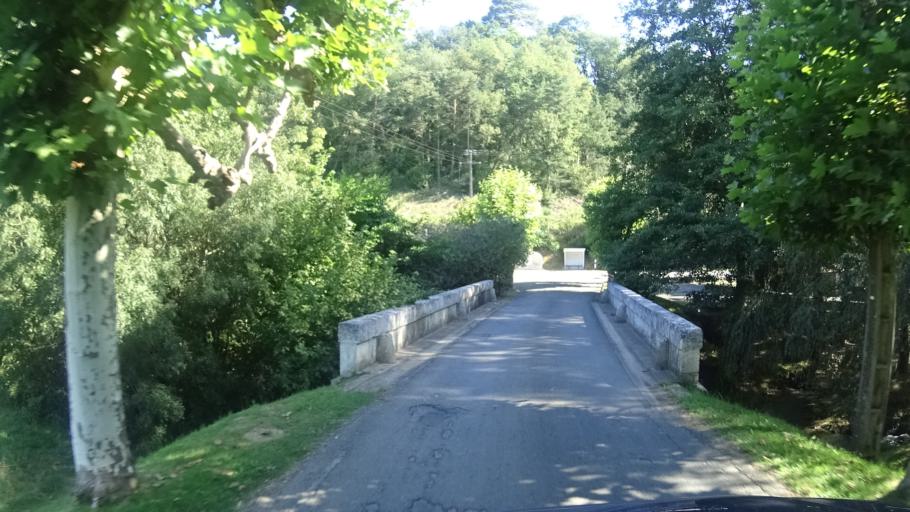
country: FR
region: Aquitaine
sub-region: Departement de la Dordogne
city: Sourzac
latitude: 45.0177
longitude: 0.4018
